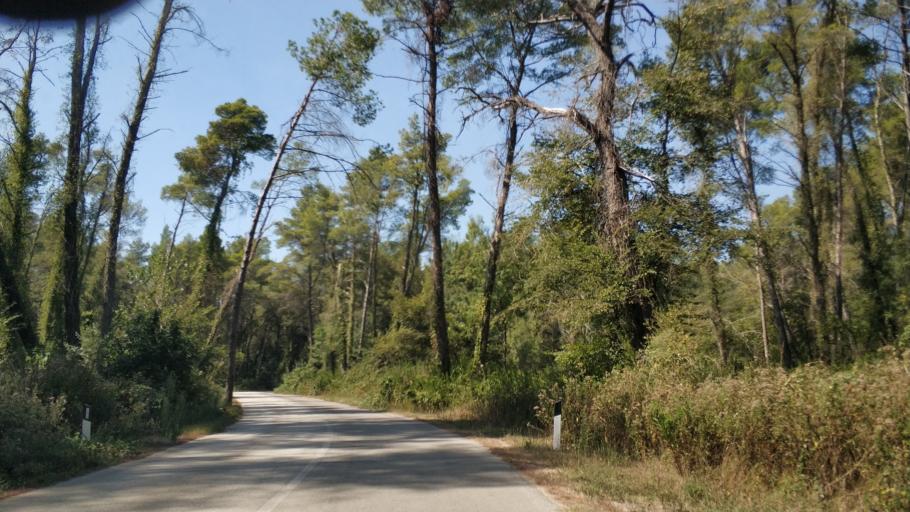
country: AL
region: Fier
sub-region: Rrethi i Lushnjes
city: Divjake
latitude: 40.9902
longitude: 19.4903
